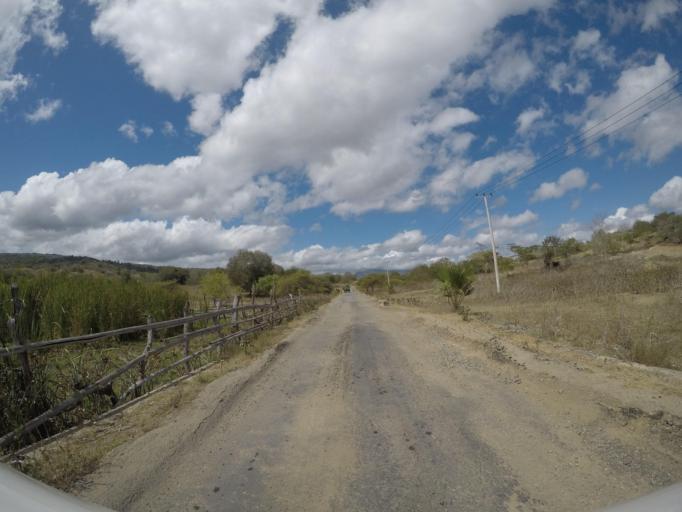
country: TL
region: Lautem
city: Lospalos
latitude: -8.4270
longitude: 126.8311
